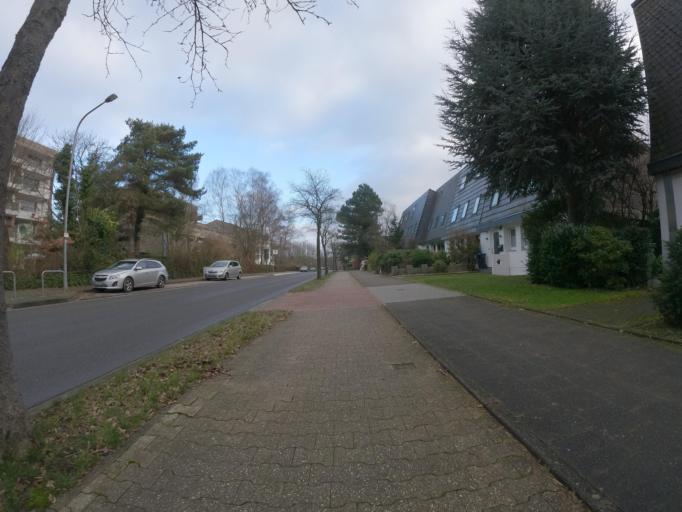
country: DE
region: North Rhine-Westphalia
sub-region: Regierungsbezirk Koln
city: Aachen
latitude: 50.8077
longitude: 6.0725
